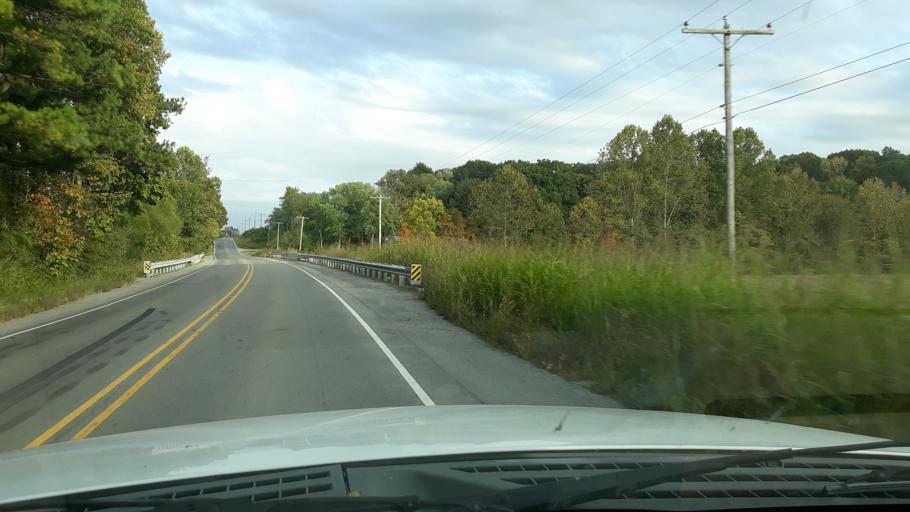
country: US
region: Illinois
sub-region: Saline County
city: Eldorado
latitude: 37.8223
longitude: -88.4962
